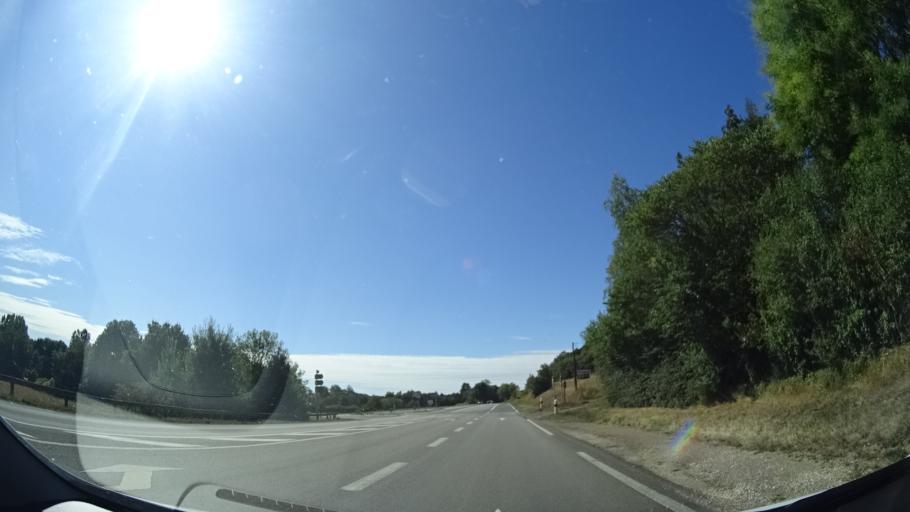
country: FR
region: Centre
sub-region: Departement du Loiret
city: Douchy
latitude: 47.9360
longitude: 3.0803
